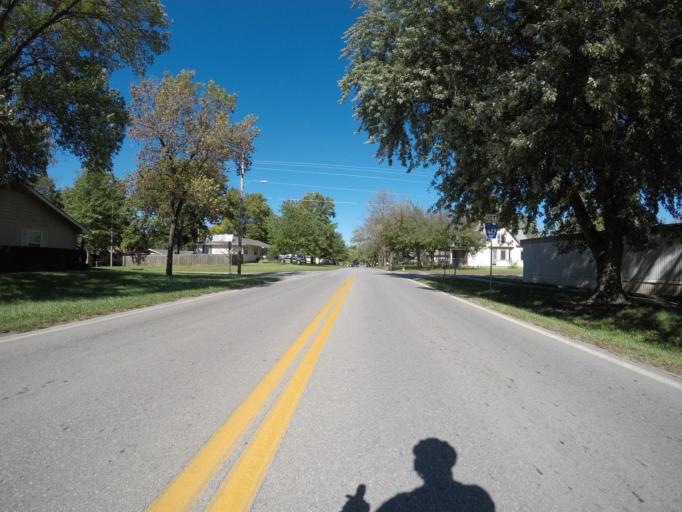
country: US
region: Kansas
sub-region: Douglas County
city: Eudora
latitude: 38.9385
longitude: -95.0960
